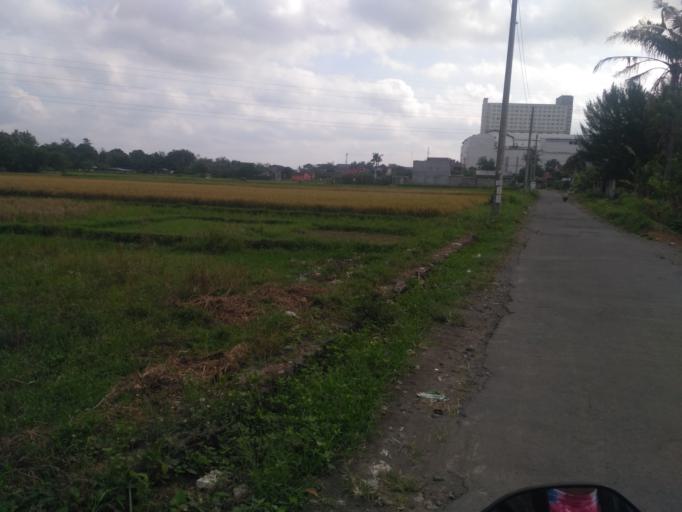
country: ID
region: Daerah Istimewa Yogyakarta
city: Yogyakarta
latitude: -7.7582
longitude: 110.3592
